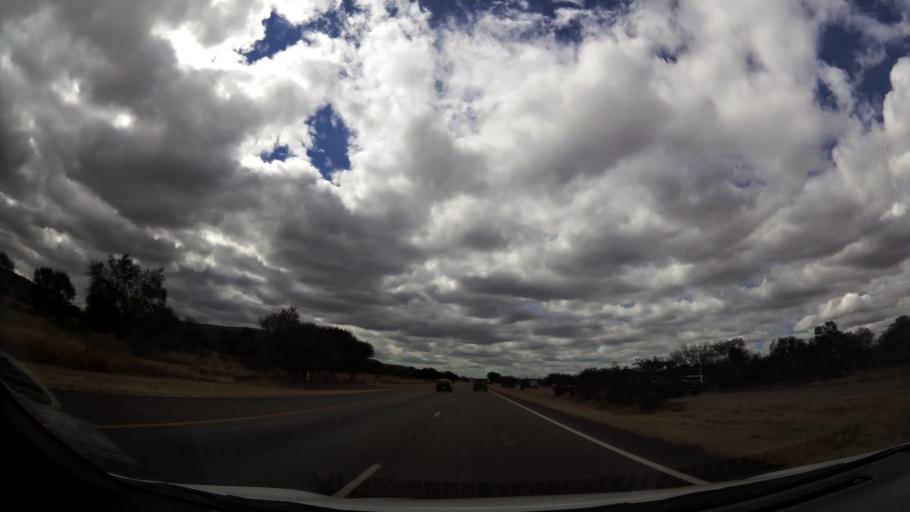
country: ZA
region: Limpopo
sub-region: Waterberg District Municipality
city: Modimolle
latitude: -24.8238
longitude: 28.4195
